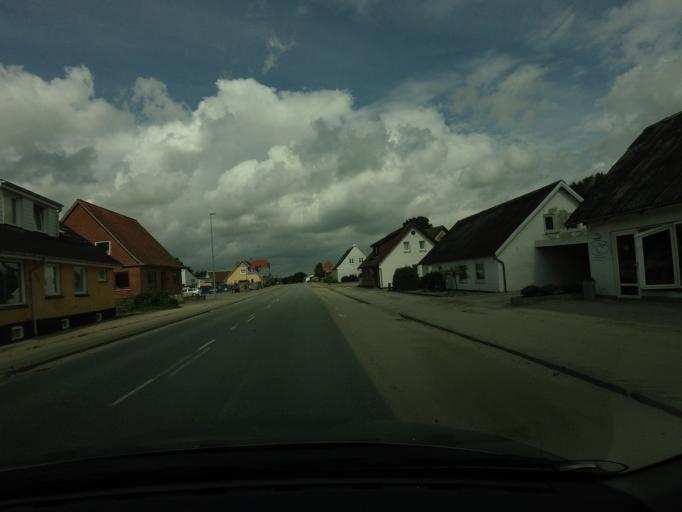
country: DK
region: North Denmark
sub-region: Hjorring Kommune
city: Tars
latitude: 57.3882
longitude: 10.1090
